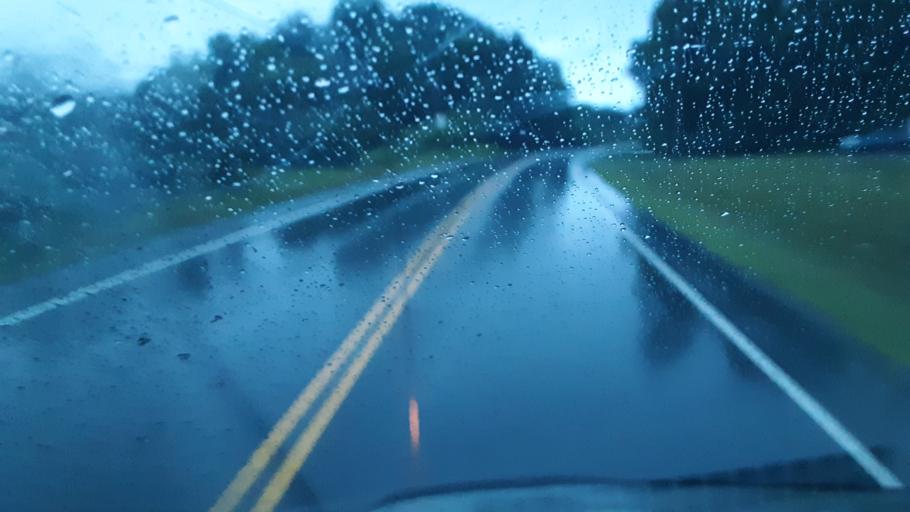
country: US
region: Maine
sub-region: Penobscot County
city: Patten
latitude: 45.9208
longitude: -68.4371
